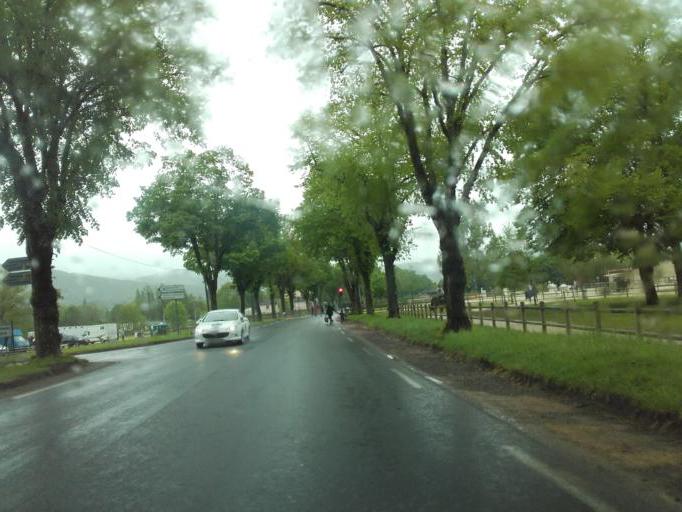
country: FR
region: Bourgogne
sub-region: Departement de Saone-et-Loire
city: Cluny
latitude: 46.4366
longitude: 4.6631
